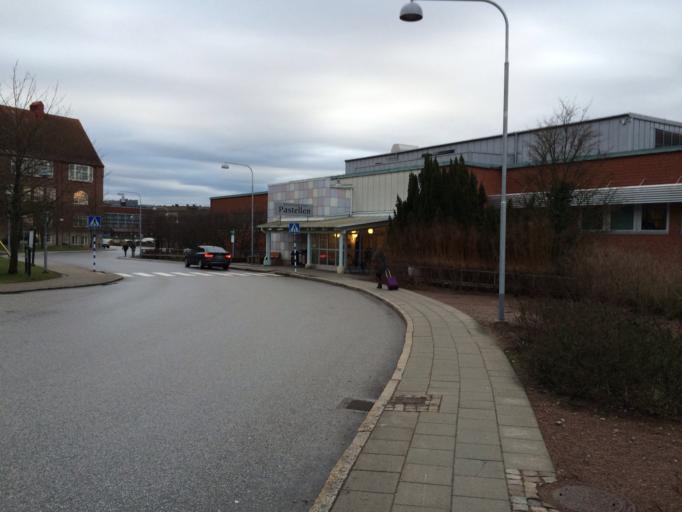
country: SE
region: Skane
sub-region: Lunds Kommun
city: Lund
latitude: 55.7136
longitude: 13.2002
